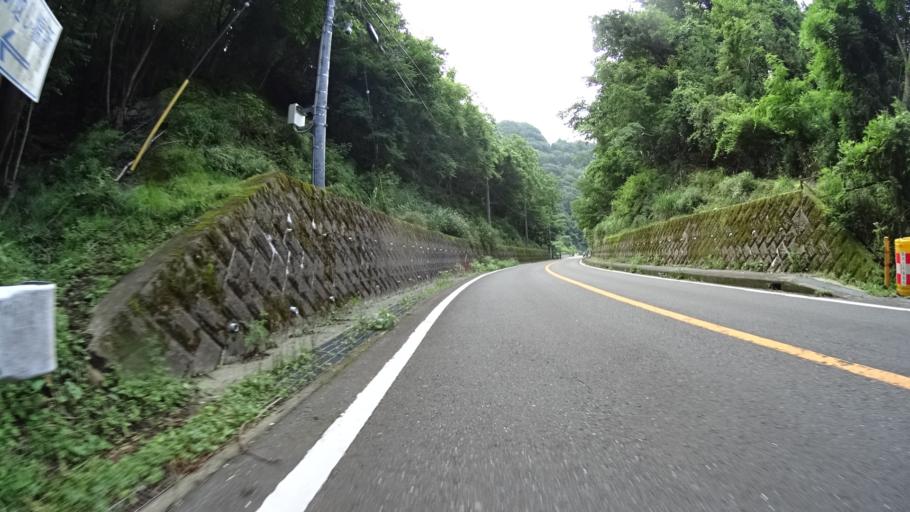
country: JP
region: Kanagawa
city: Hadano
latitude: 35.5025
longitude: 139.2301
